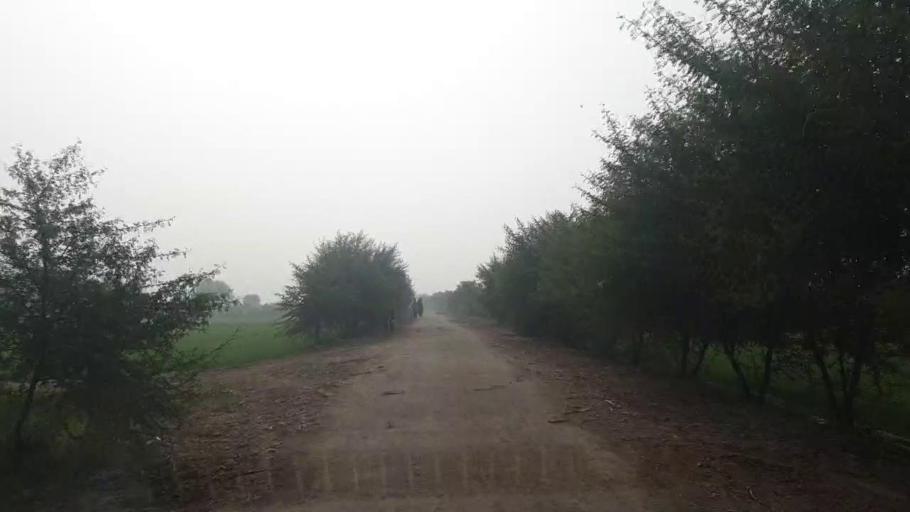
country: PK
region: Sindh
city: Bhit Shah
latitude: 25.7931
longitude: 68.5737
